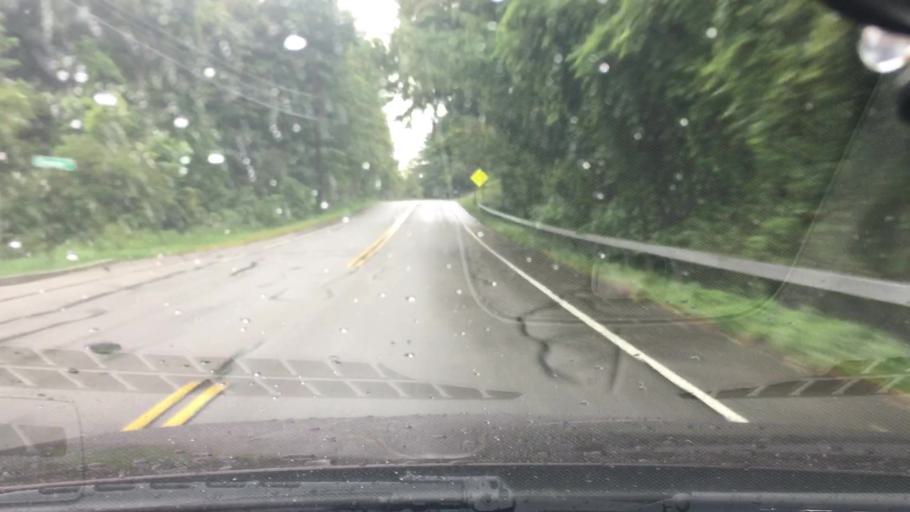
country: US
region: New York
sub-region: Dutchess County
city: Brinckerhoff
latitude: 41.5586
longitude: -73.8223
